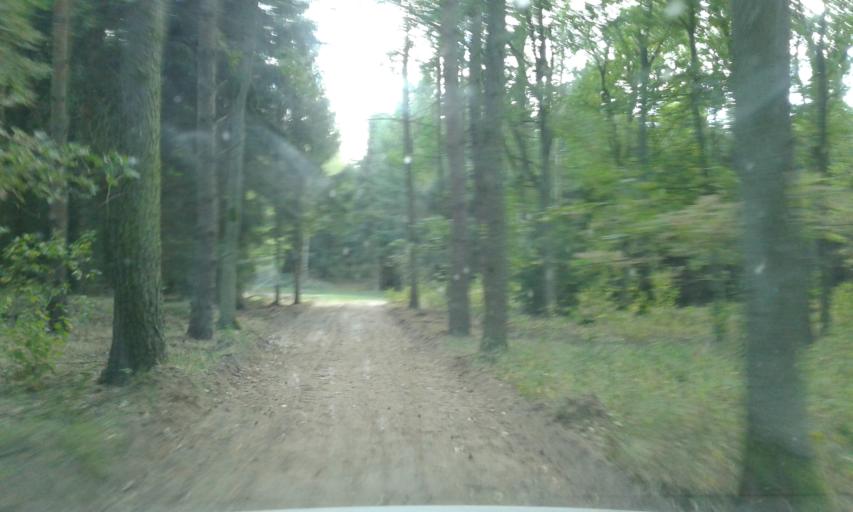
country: PL
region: West Pomeranian Voivodeship
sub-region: Powiat stargardzki
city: Dolice
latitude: 53.2299
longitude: 15.2462
